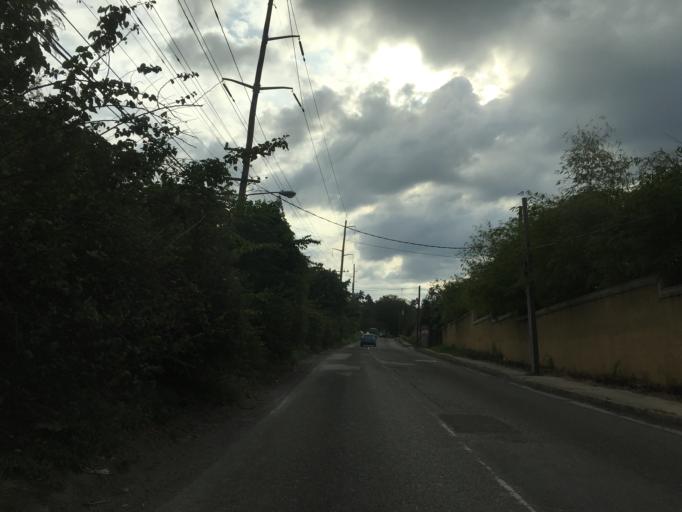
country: JM
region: Saint James
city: Montego Bay
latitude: 18.4928
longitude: -77.9188
